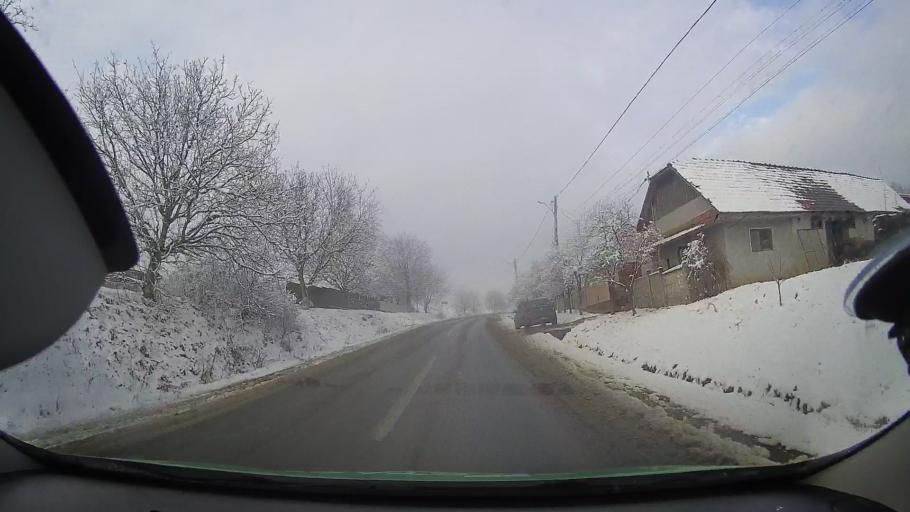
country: RO
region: Mures
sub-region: Comuna Atintis
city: Atintis
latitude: 46.4372
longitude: 24.0941
